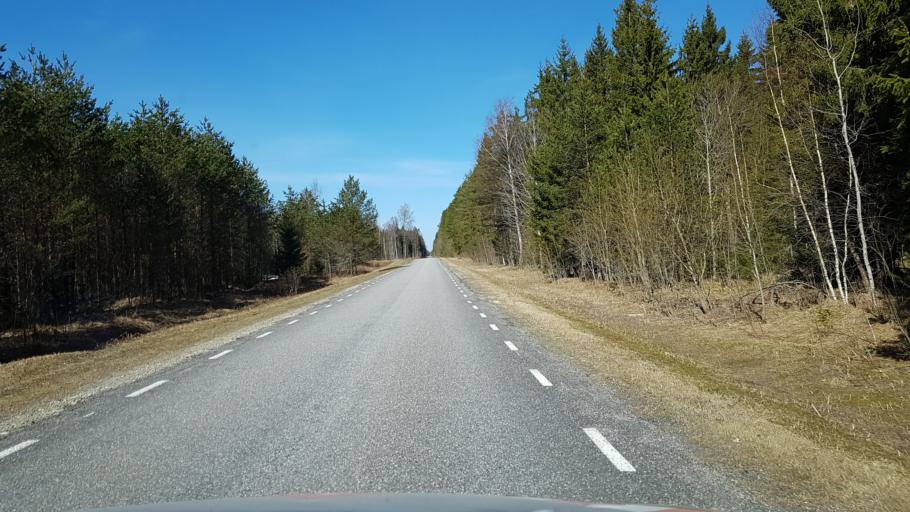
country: EE
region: Laeaene-Virumaa
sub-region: Vinni vald
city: Vinni
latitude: 59.1426
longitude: 26.5233
